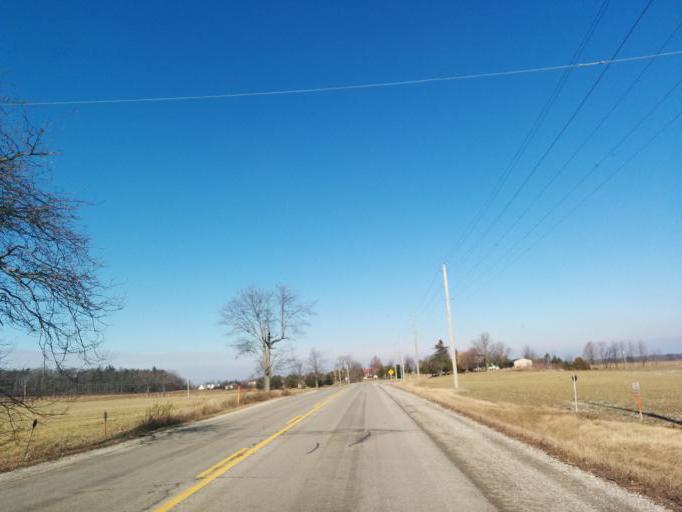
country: CA
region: Ontario
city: Brant
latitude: 43.0167
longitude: -80.3259
